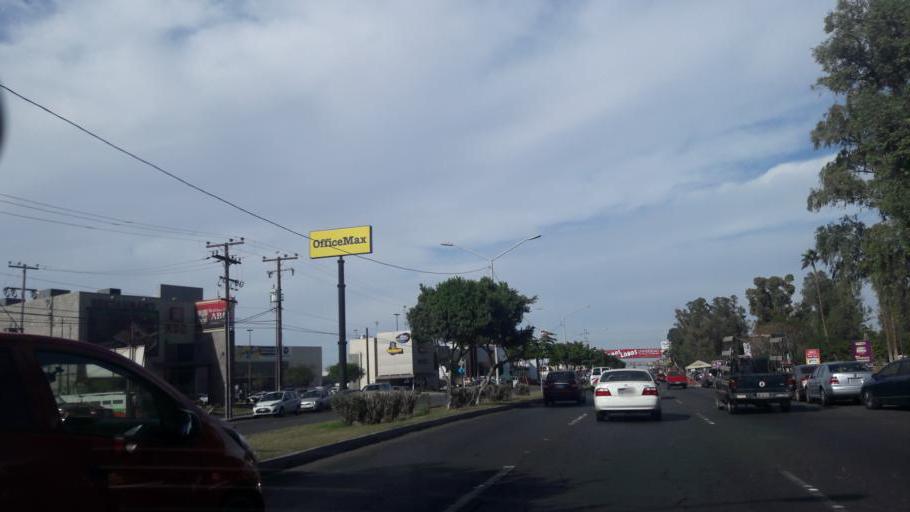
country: MX
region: Baja California
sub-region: Mexicali
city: Mexicali
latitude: 32.6313
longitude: -115.4462
